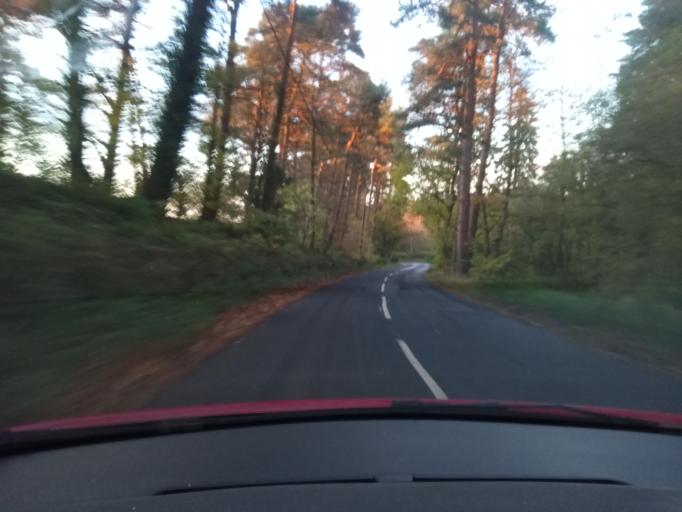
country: GB
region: England
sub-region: Northumberland
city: Bardon Mill
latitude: 54.9455
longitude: -2.2699
